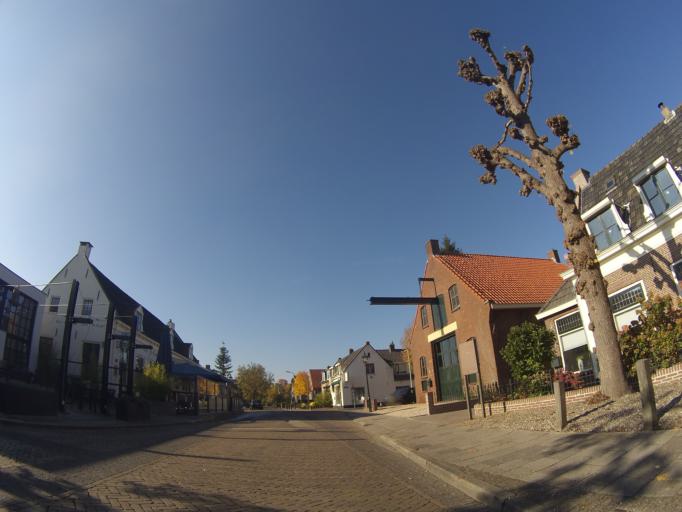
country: NL
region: Utrecht
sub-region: Gemeente Houten
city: Houten
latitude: 52.0277
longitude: 5.1611
